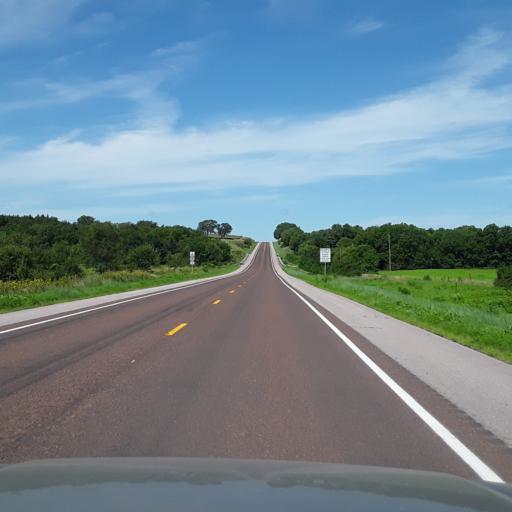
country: US
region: Nebraska
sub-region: Seward County
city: Milford
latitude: 40.8865
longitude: -96.9112
